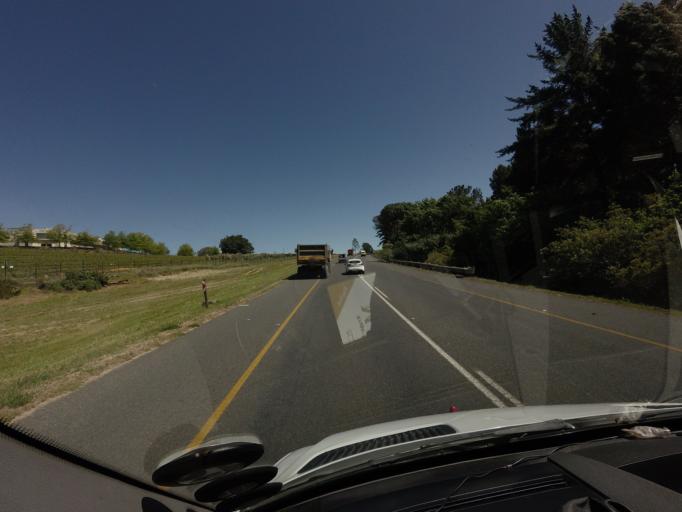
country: ZA
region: Western Cape
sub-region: Cape Winelands District Municipality
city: Stellenbosch
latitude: -33.8882
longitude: 18.8514
